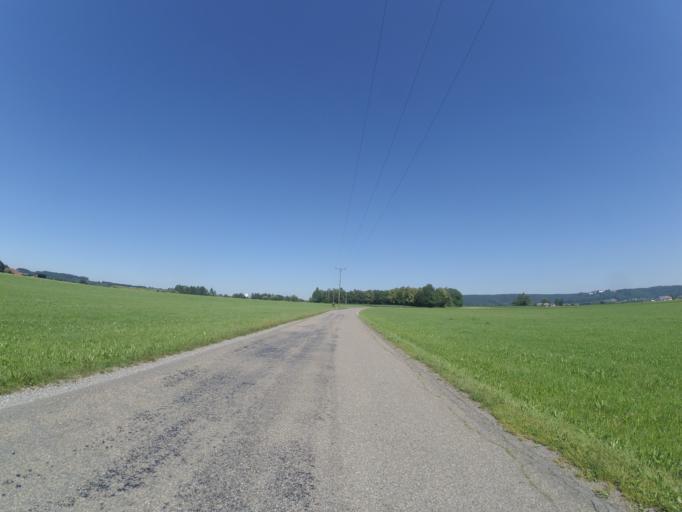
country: DE
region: Baden-Wuerttemberg
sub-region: Tuebingen Region
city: Leutkirch im Allgau
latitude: 47.8357
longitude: 10.0056
